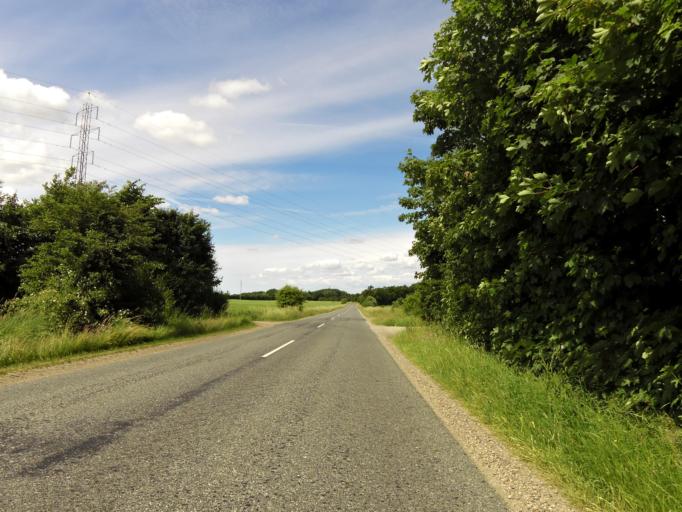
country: DK
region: South Denmark
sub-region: Esbjerg Kommune
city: Ribe
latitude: 55.2728
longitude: 8.8047
